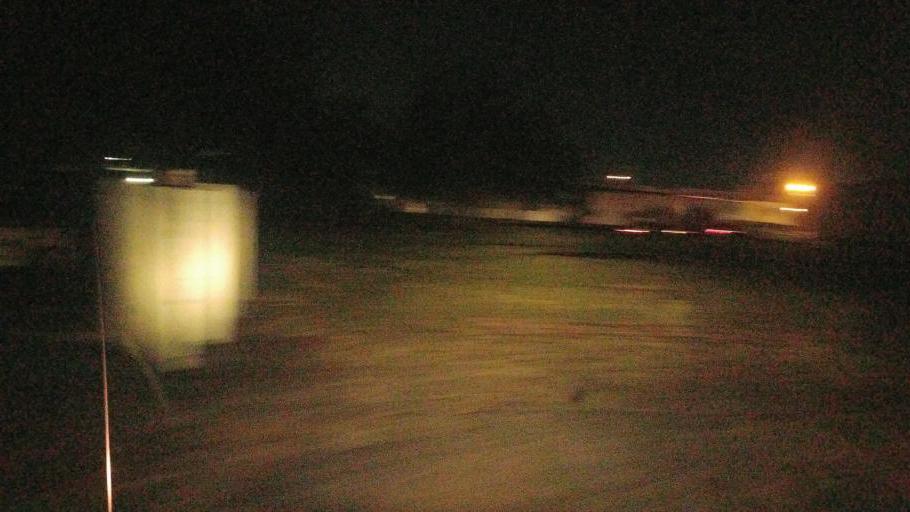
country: US
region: Florida
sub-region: Osceola County
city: Kissimmee
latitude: 28.3166
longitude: -81.4668
